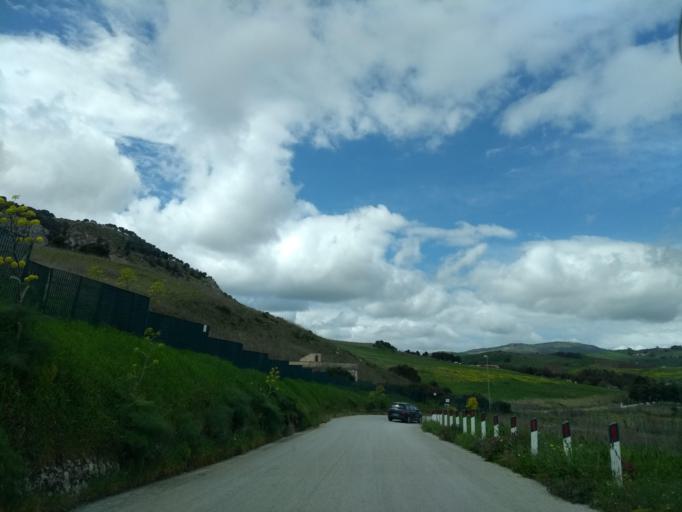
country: IT
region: Sicily
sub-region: Trapani
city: Calatafimi
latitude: 37.9431
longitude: 12.8353
